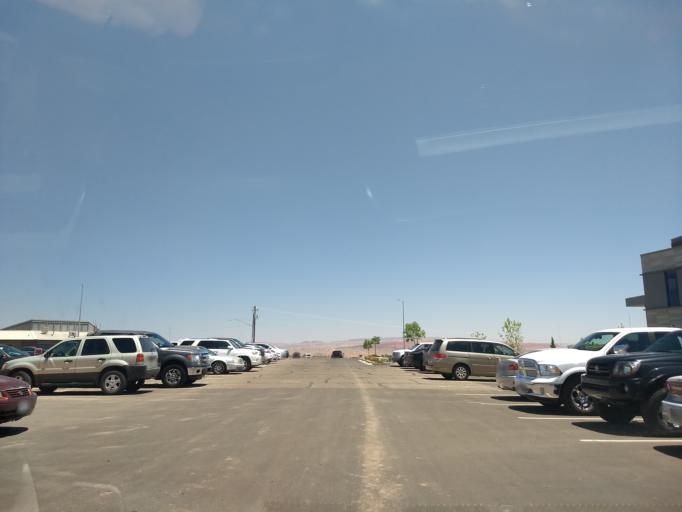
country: US
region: Utah
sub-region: Washington County
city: Saint George
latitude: 37.0990
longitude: -113.5922
